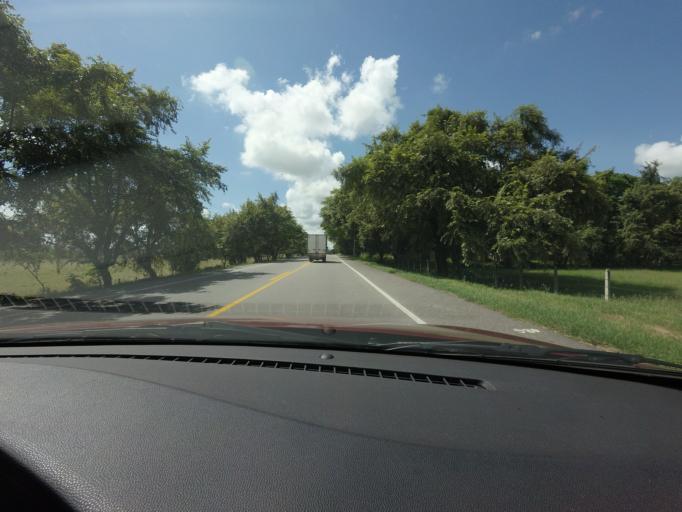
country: CO
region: Tolima
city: Saldana
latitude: 3.9489
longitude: -75.0083
